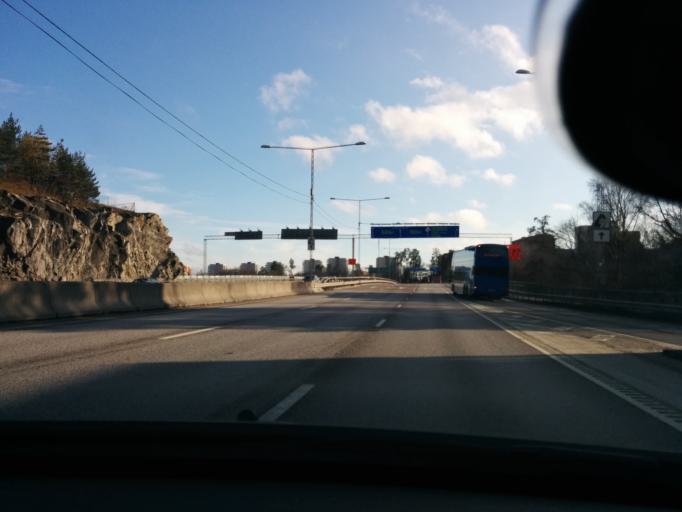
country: SE
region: Stockholm
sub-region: Norrtalje Kommun
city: Bergshamra
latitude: 59.3845
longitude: 18.0425
